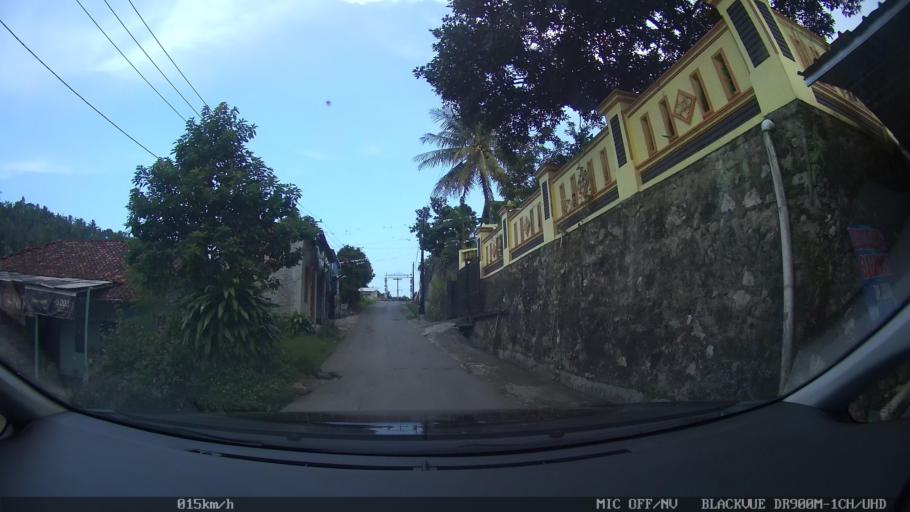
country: ID
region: Lampung
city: Kedaton
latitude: -5.3981
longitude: 105.2176
